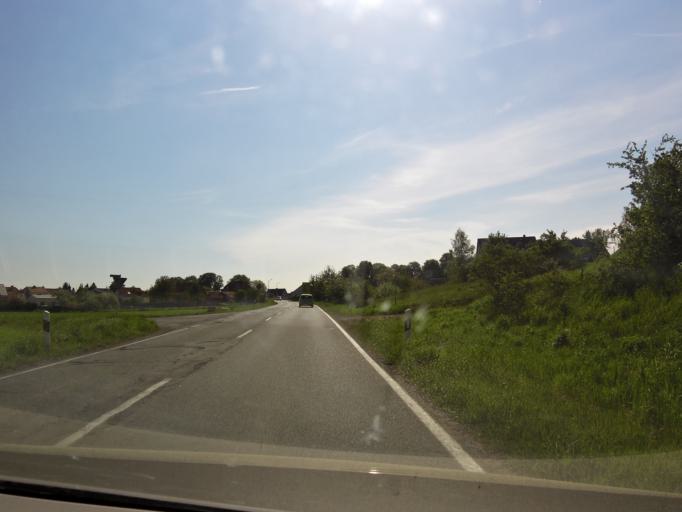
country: DE
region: Thuringia
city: Elxleben
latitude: 51.0341
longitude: 10.9649
